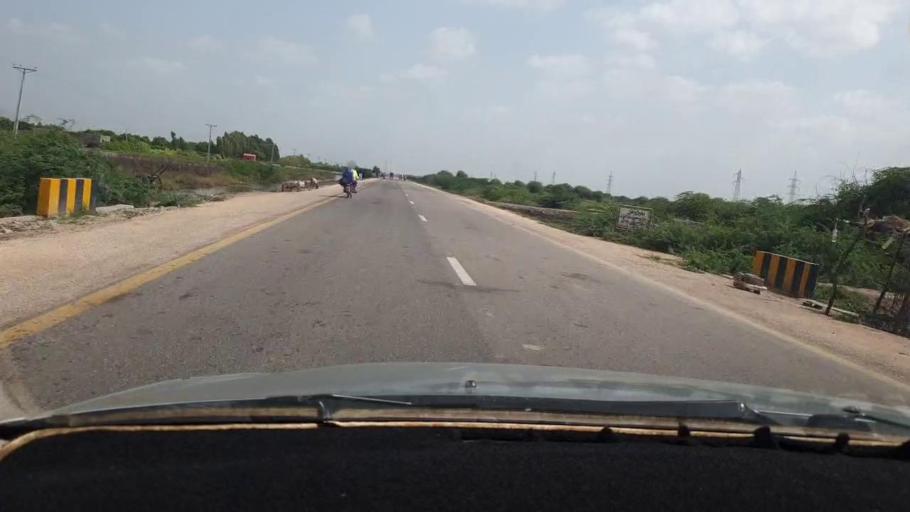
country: PK
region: Sindh
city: Digri
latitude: 25.0431
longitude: 69.2319
